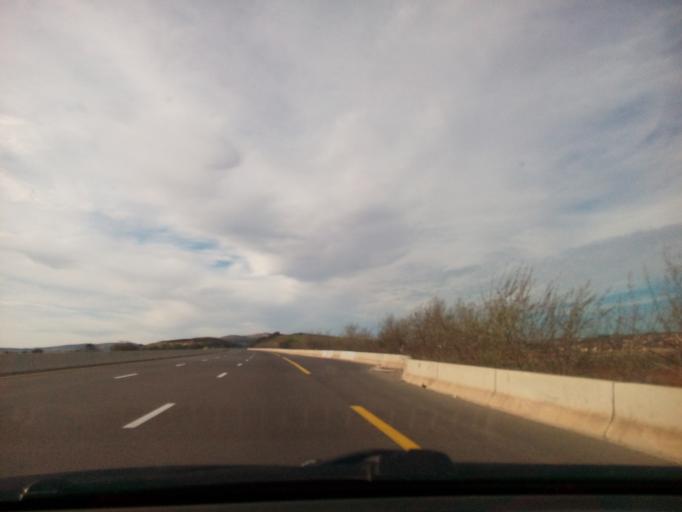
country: DZ
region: Sidi Bel Abbes
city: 'Ain el Berd
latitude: 35.4516
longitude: -0.3950
